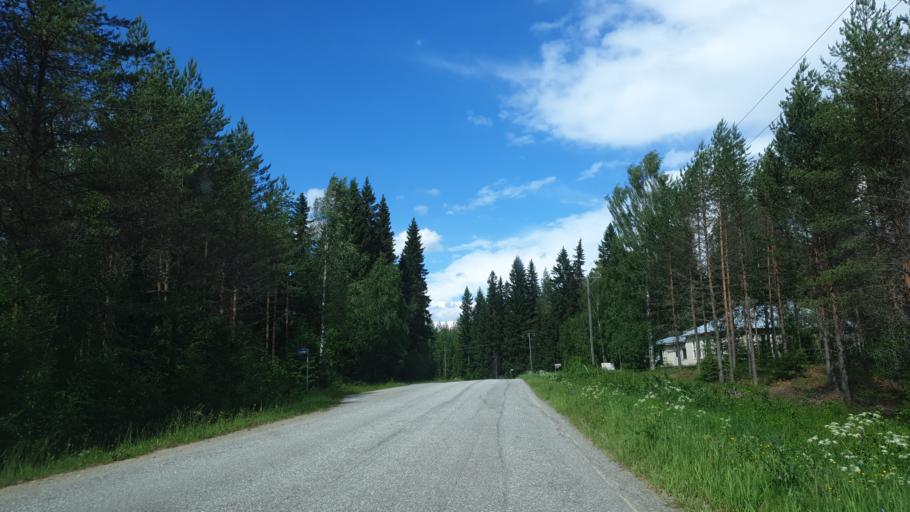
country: FI
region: Northern Savo
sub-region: Koillis-Savo
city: Kaavi
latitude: 63.0167
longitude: 28.6523
